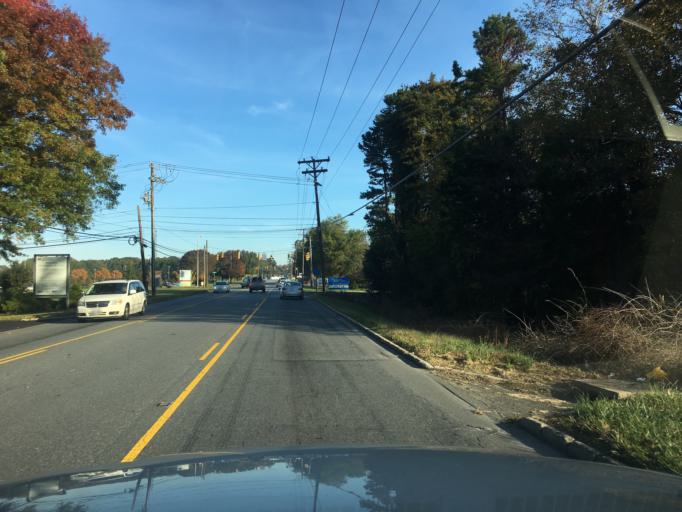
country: US
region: North Carolina
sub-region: Catawba County
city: Conover
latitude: 35.7118
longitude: -81.2648
